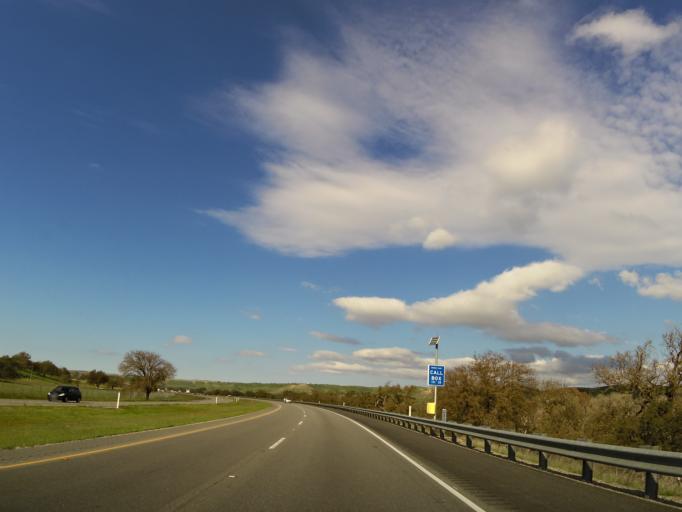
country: US
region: California
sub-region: San Luis Obispo County
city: San Miguel
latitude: 35.8410
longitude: -120.7578
